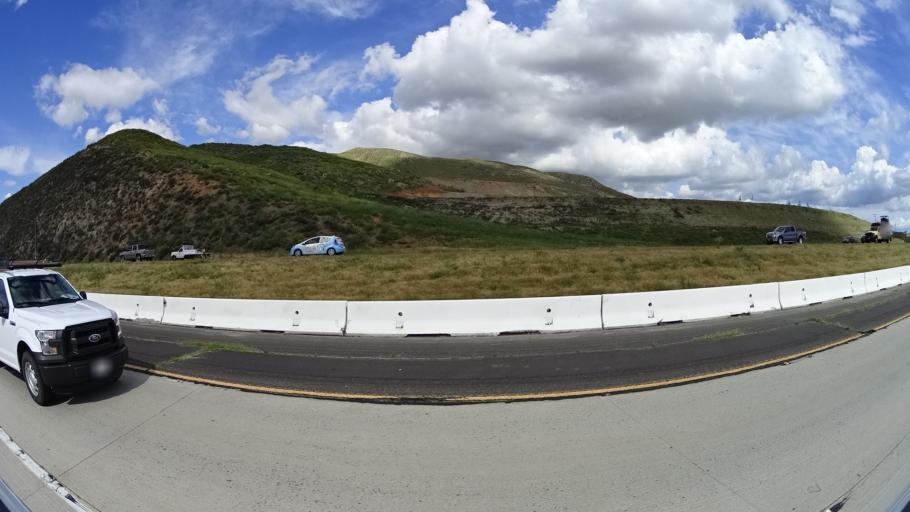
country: US
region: California
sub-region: Riverside County
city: Lake Elsinore
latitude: 33.7106
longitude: -117.3601
